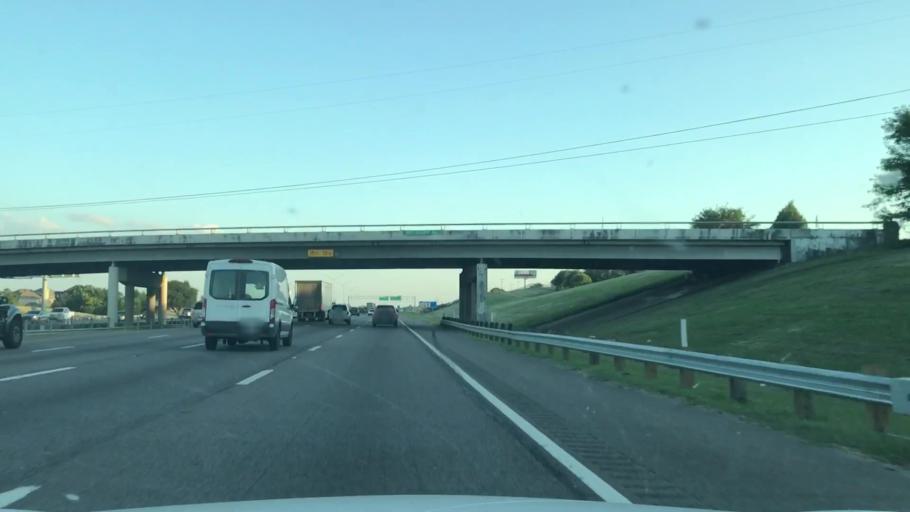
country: US
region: Texas
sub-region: Dallas County
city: Mesquite
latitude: 32.7565
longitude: -96.6177
